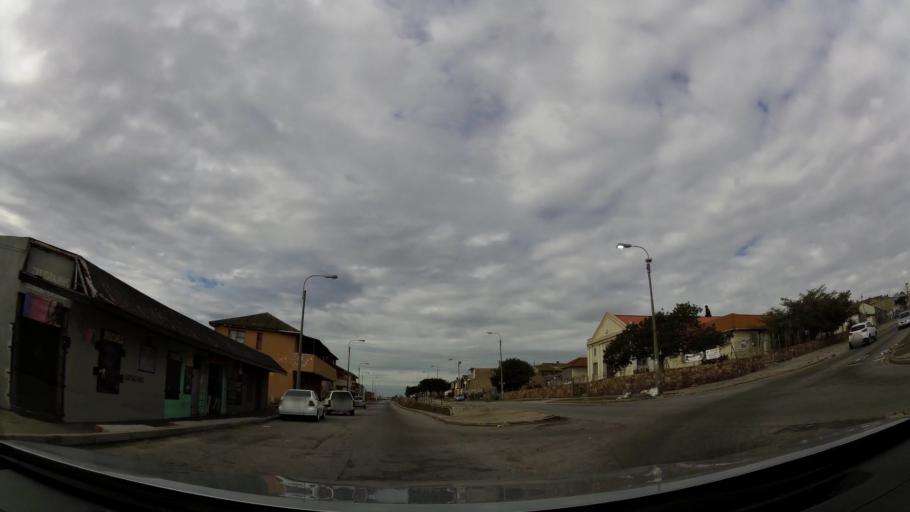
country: ZA
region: Eastern Cape
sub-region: Nelson Mandela Bay Metropolitan Municipality
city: Port Elizabeth
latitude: -33.9330
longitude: 25.5758
